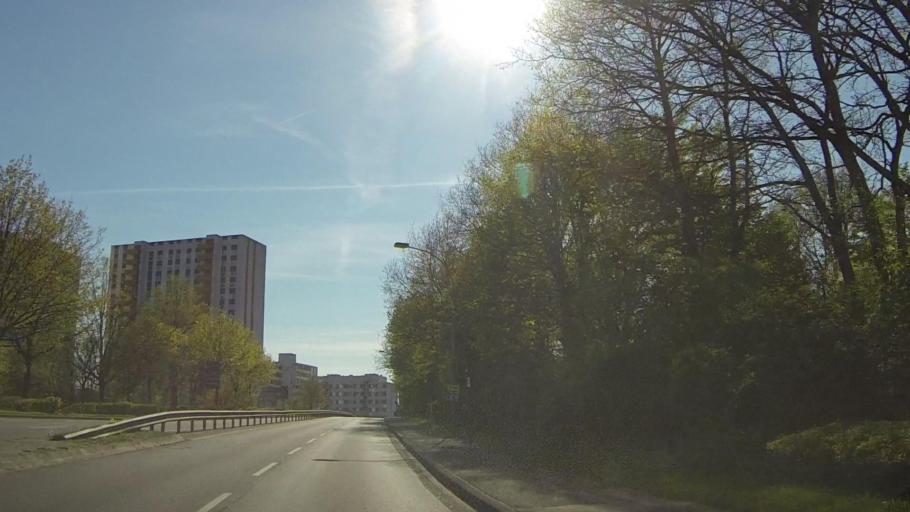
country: DE
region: Schleswig-Holstein
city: Rellingen
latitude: 53.6454
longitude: 9.8155
